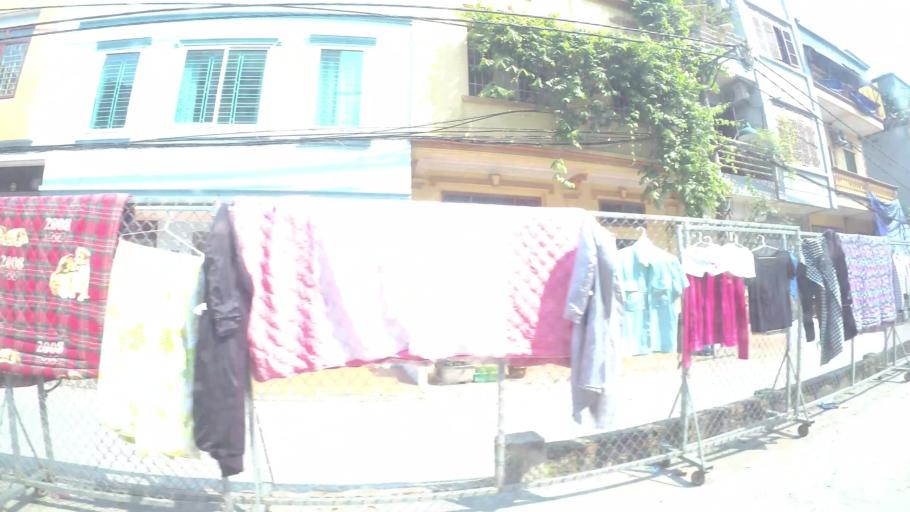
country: VN
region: Ha Noi
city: Ha Dong
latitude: 20.9598
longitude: 105.8011
